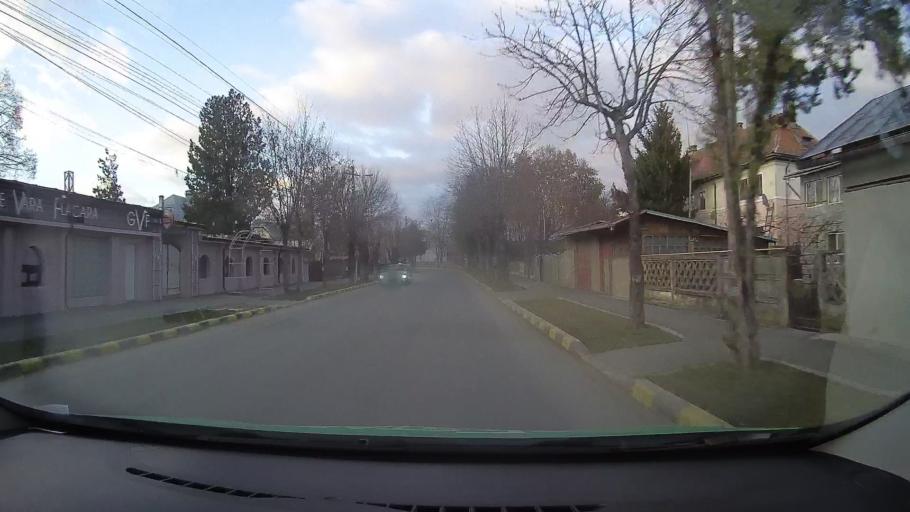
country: RO
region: Dambovita
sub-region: Municipiul Moreni
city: Moreni
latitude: 44.9833
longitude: 25.6394
